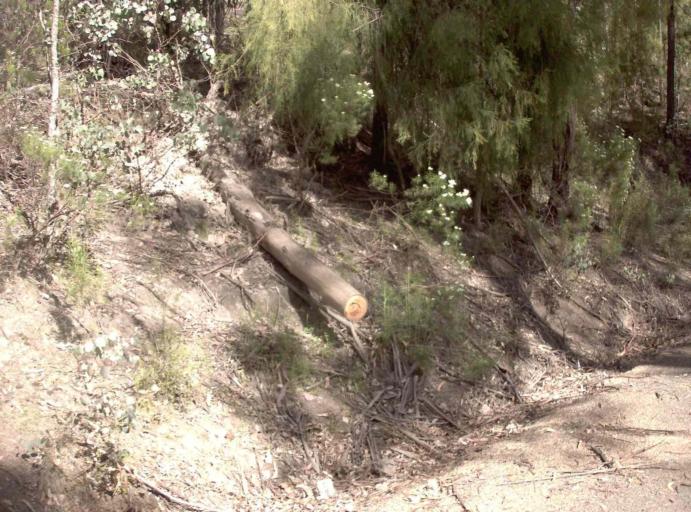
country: AU
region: Victoria
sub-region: East Gippsland
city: Lakes Entrance
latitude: -37.4223
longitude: 148.1279
